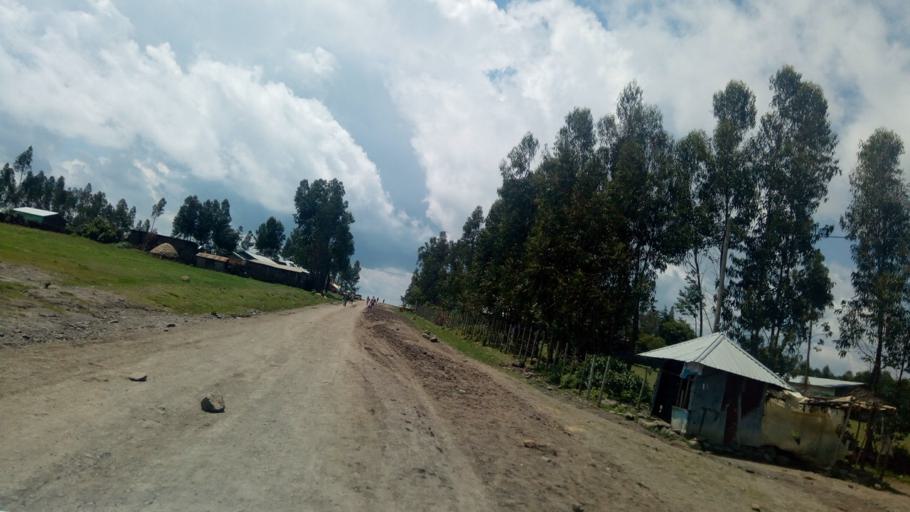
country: ET
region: Oromiya
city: Sendafa
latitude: 9.0000
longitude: 39.1269
